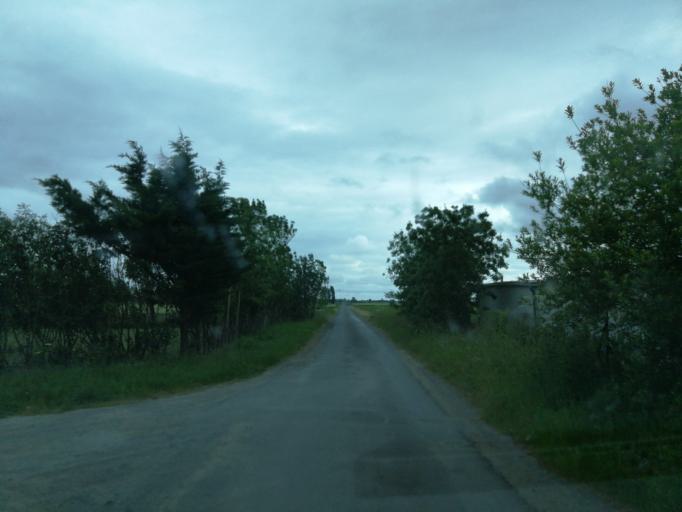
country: FR
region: Poitou-Charentes
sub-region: Departement de la Charente-Maritime
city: Marans
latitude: 46.3581
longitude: -0.9385
